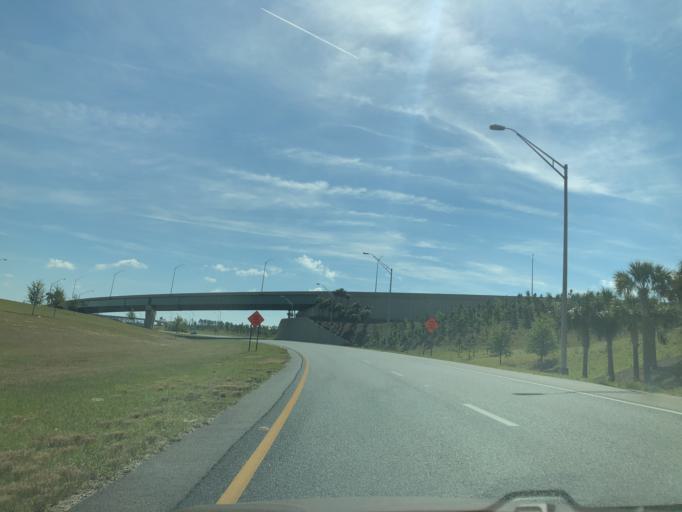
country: US
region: Florida
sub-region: Orange County
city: Paradise Heights
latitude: 28.6525
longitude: -81.5444
